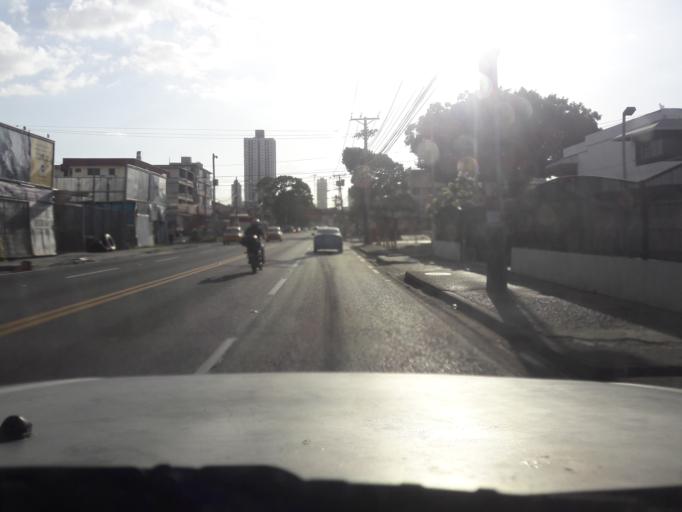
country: PA
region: Panama
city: Panama
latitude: 9.0144
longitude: -79.4995
